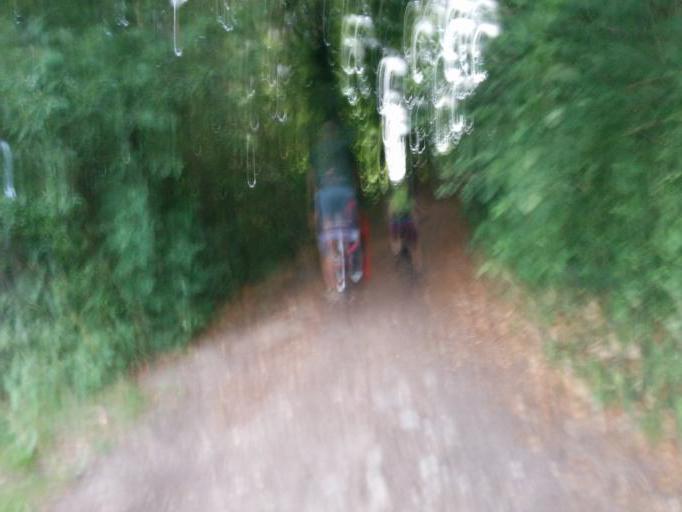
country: AT
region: Lower Austria
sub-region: Politischer Bezirk Modling
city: Gumpoldskirchen
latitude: 48.0514
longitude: 16.2668
